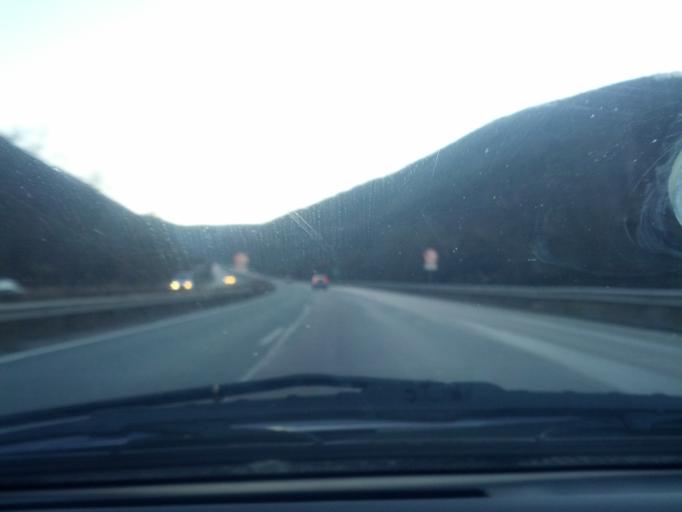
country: BG
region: Sofiya
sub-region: Obshtina Botevgrad
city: Botevgrad
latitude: 42.8777
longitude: 23.8020
